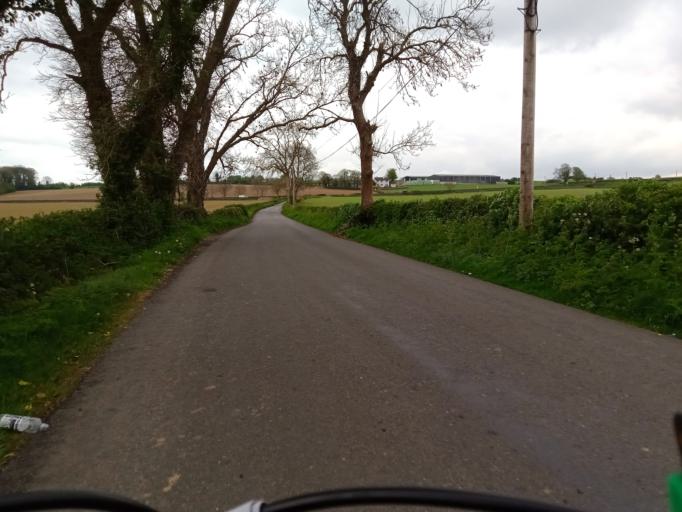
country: IE
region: Leinster
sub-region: Kilkenny
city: Kilkenny
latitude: 52.6184
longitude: -7.2522
